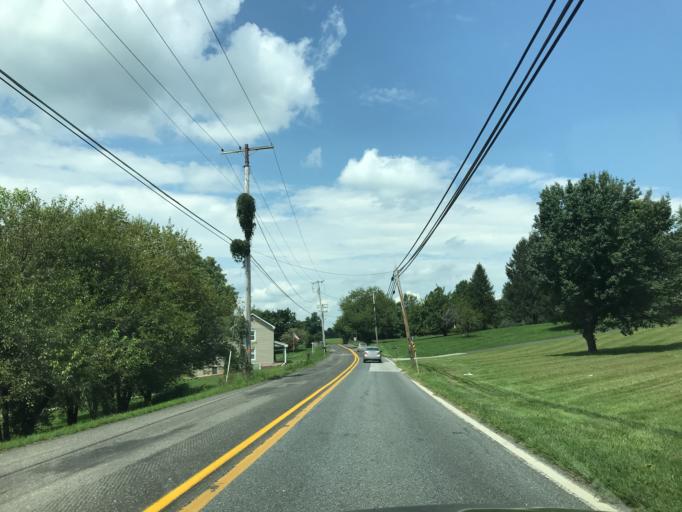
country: US
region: Pennsylvania
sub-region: York County
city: New Freedom
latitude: 39.6692
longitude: -76.7142
